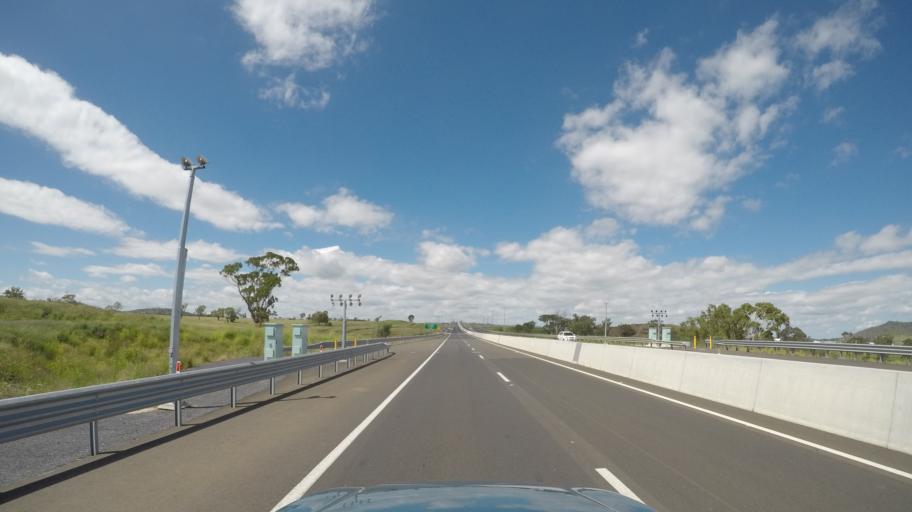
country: AU
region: Queensland
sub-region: Toowoomba
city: Wilsonton Heights
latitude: -27.5160
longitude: 151.8659
